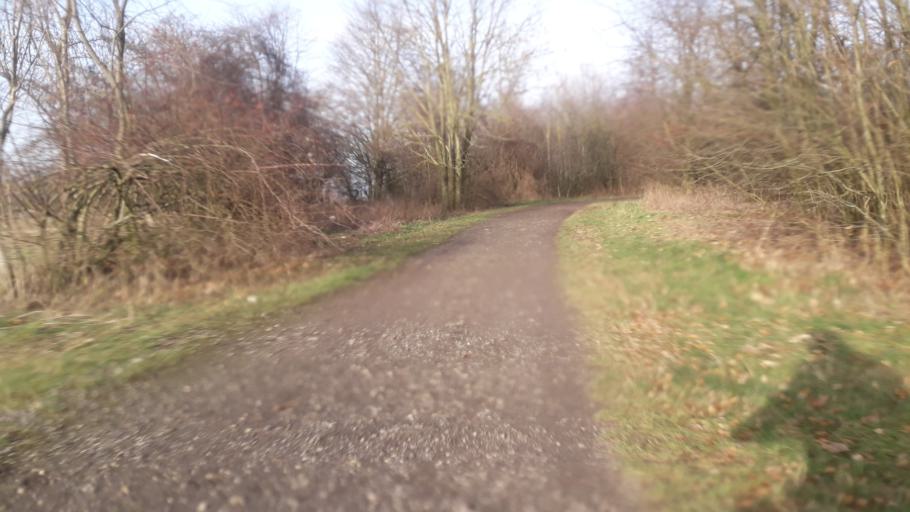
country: DE
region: North Rhine-Westphalia
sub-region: Regierungsbezirk Detmold
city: Paderborn
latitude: 51.6888
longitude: 8.7523
